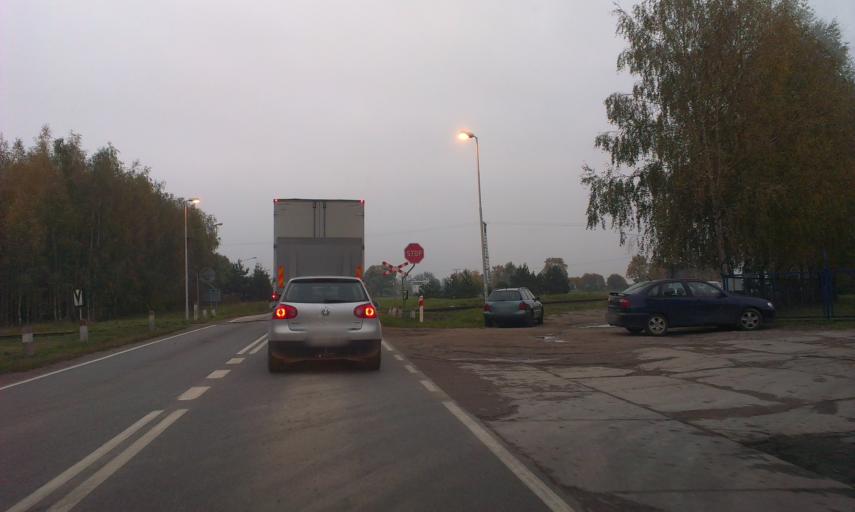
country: PL
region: Kujawsko-Pomorskie
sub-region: Powiat sepolenski
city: Sepolno Krajenskie
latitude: 53.4376
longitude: 17.5473
